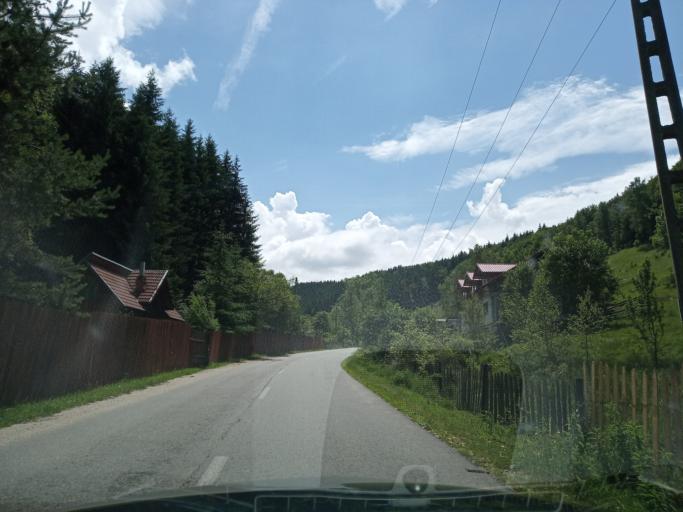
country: RO
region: Hunedoara
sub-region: Oras Petrila
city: Petrila
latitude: 45.3997
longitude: 23.4164
